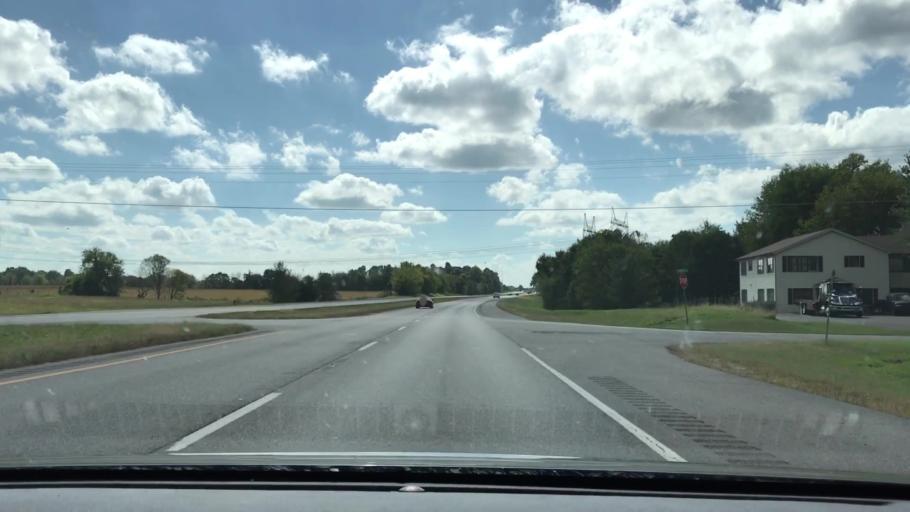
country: US
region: Kentucky
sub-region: McCracken County
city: Reidland
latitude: 37.0046
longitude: -88.5074
